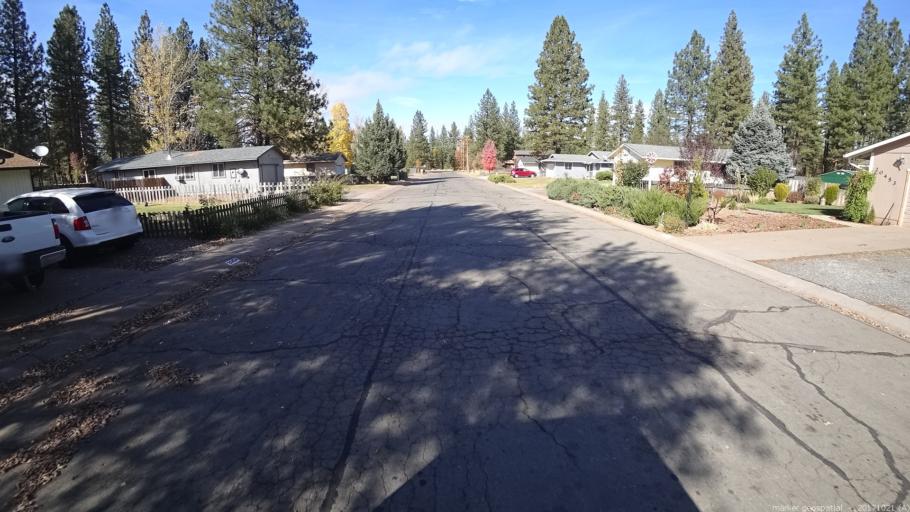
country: US
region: California
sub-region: Shasta County
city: Burney
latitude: 40.8834
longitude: -121.6478
